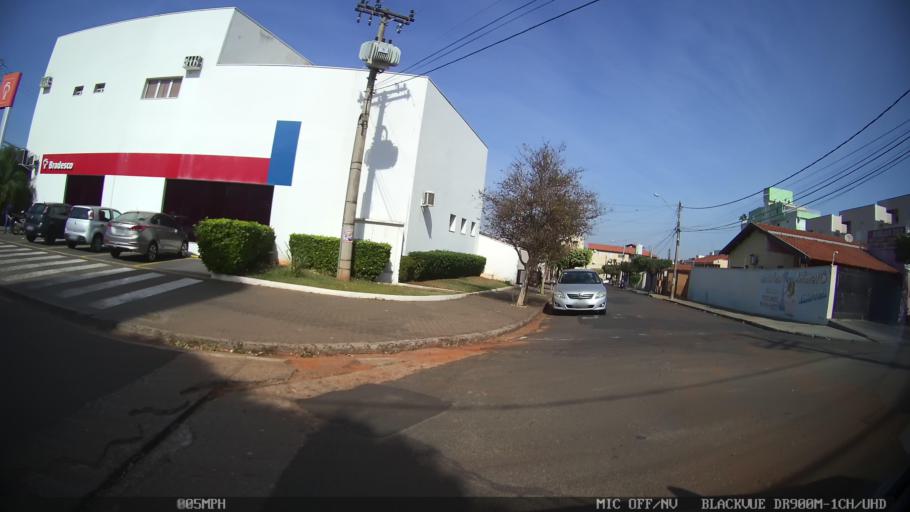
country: BR
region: Sao Paulo
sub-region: Sao Jose Do Rio Preto
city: Sao Jose do Rio Preto
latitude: -20.7980
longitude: -49.4121
